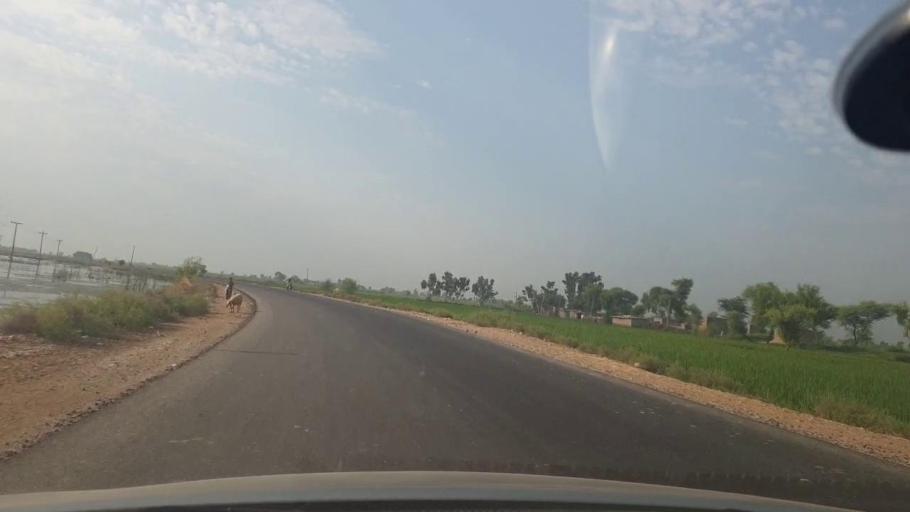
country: PK
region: Sindh
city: Jacobabad
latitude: 28.1034
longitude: 68.3259
